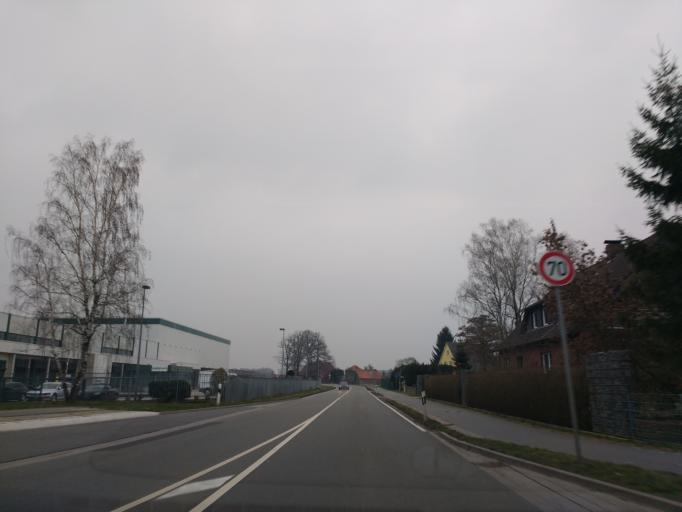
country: DE
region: North Rhine-Westphalia
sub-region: Regierungsbezirk Munster
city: Lotte
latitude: 52.2856
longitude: 7.9268
